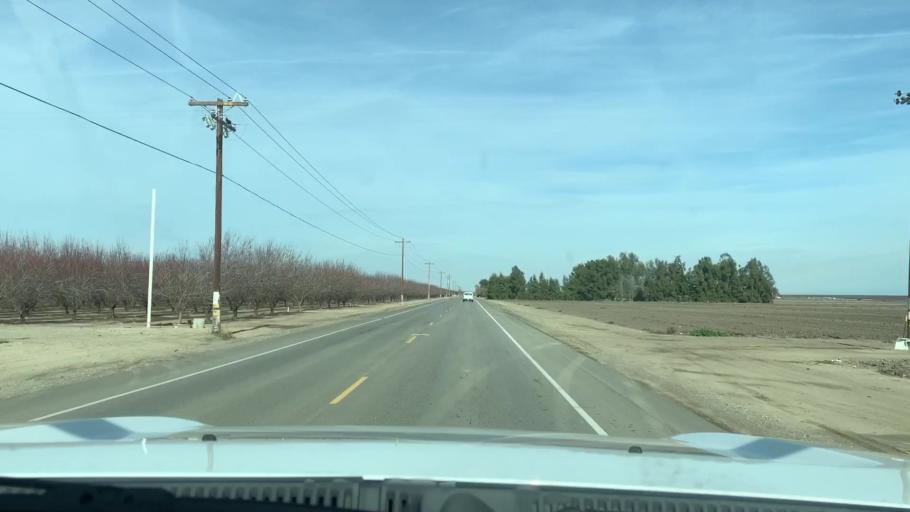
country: US
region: California
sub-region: Kern County
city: Buttonwillow
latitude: 35.5076
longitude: -119.4747
